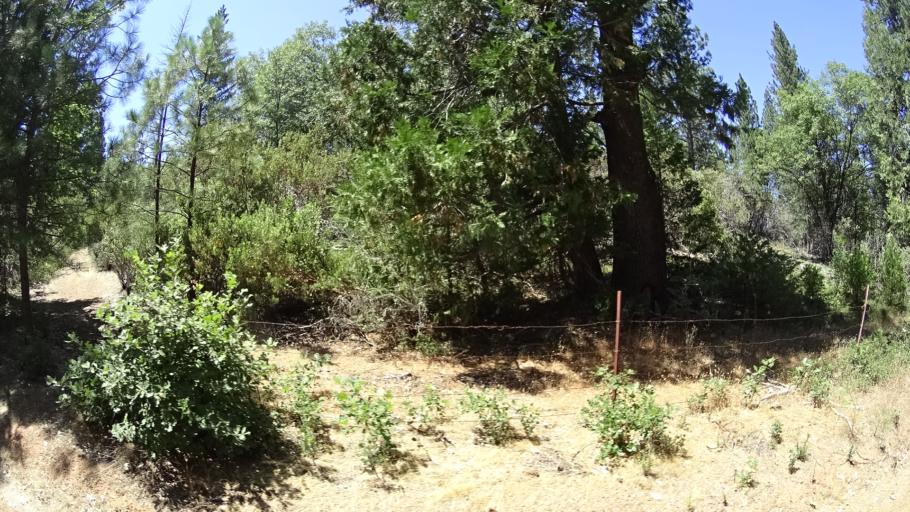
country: US
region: California
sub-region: Calaveras County
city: Mountain Ranch
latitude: 38.3170
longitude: -120.5415
